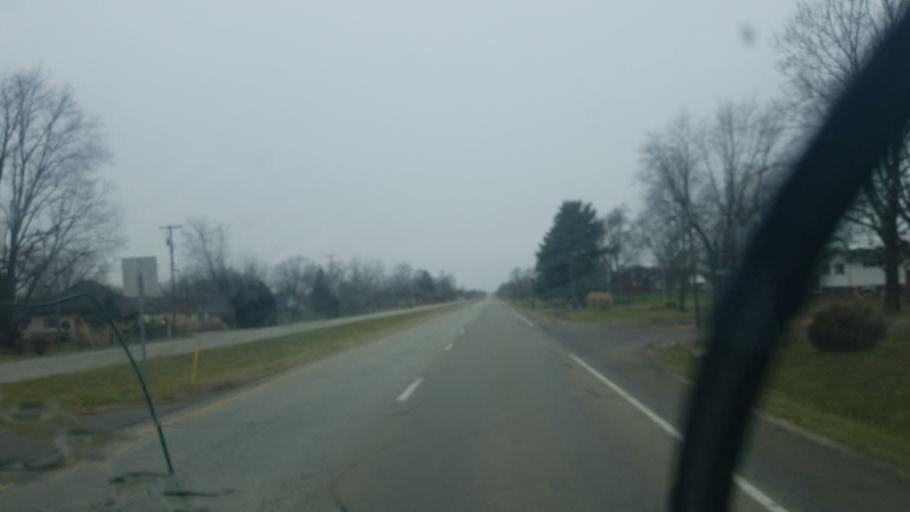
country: US
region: Indiana
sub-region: Hancock County
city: Greenfield
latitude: 39.7885
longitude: -85.6972
